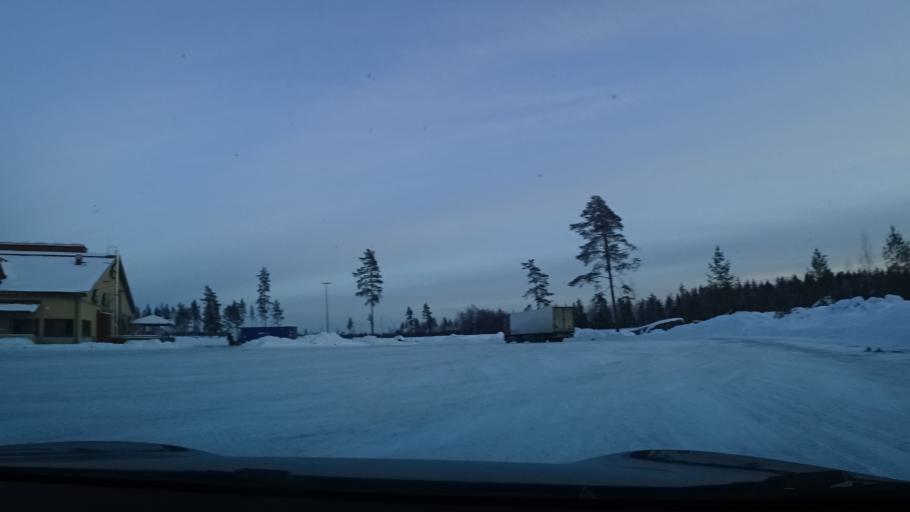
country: FI
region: Kymenlaakso
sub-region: Kotka-Hamina
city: Pyhtaeae
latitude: 60.4889
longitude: 26.5560
